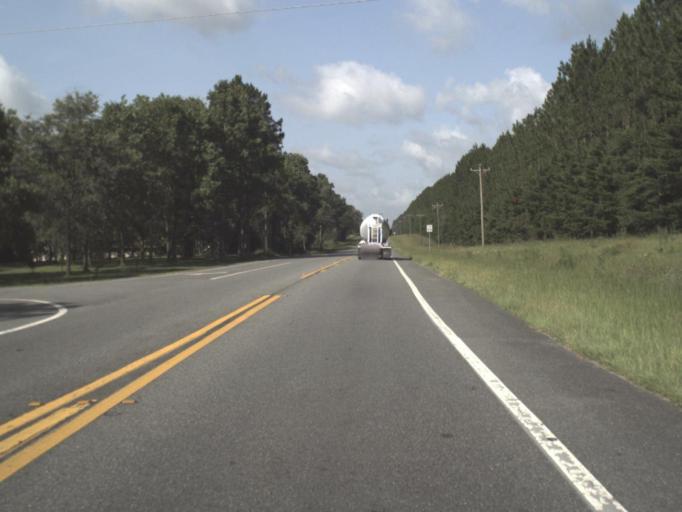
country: US
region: Florida
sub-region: Columbia County
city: Lake City
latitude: 30.1164
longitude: -82.7303
